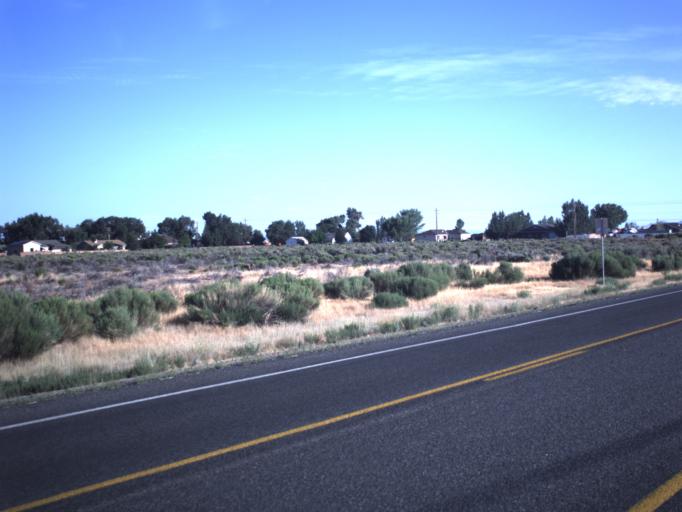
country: US
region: Utah
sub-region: Iron County
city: Enoch
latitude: 37.7622
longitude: -113.0552
